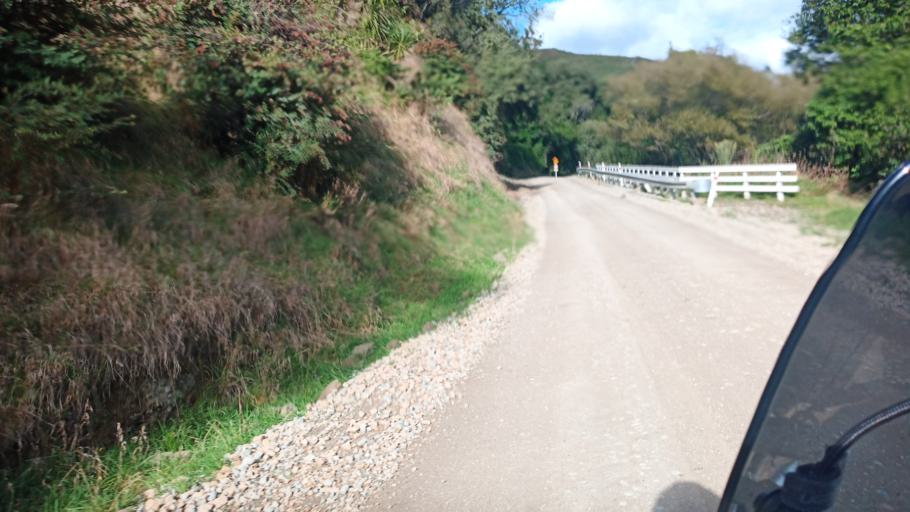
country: NZ
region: Gisborne
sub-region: Gisborne District
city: Gisborne
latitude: -38.5342
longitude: 177.5293
